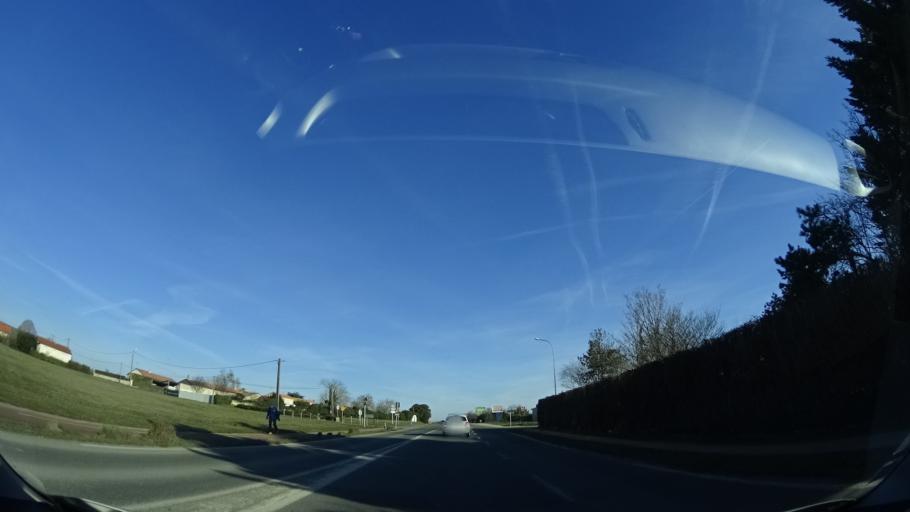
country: FR
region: Poitou-Charentes
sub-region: Departement de la Vienne
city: Jaunay-Clan
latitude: 46.6757
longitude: 0.3655
